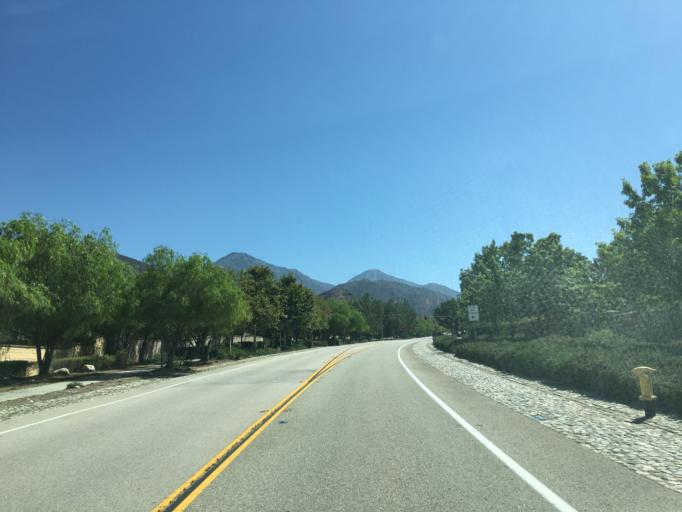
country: US
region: California
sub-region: San Bernardino County
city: San Antonio Heights
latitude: 34.1467
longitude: -117.7004
